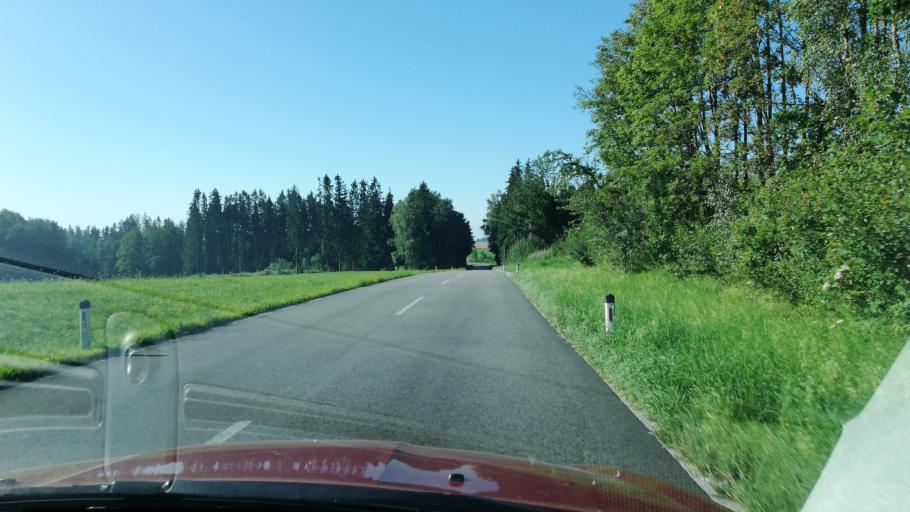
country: AT
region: Upper Austria
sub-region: Politischer Bezirk Rohrbach
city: Kleinzell im Muehlkreis
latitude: 48.4614
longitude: 14.0506
